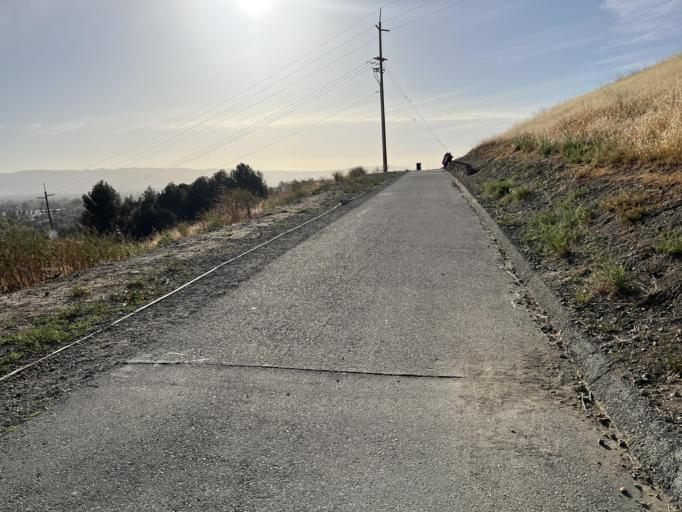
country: US
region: California
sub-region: Santa Clara County
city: Seven Trees
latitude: 37.2833
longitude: -121.8586
